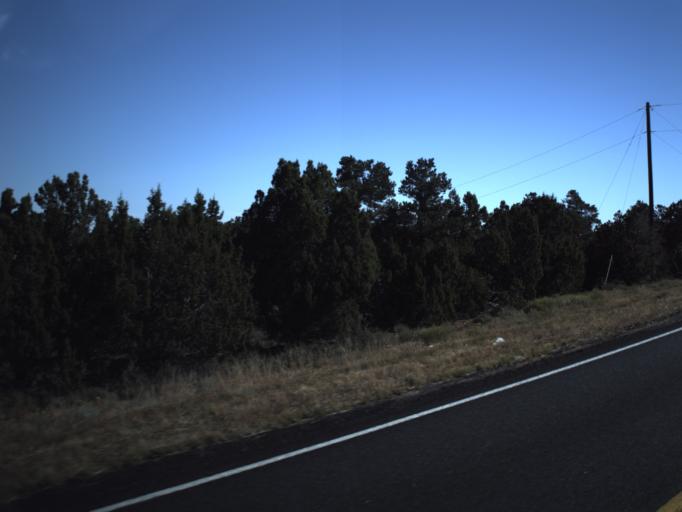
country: US
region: Utah
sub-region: Iron County
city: Cedar City
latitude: 37.6087
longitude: -113.3645
